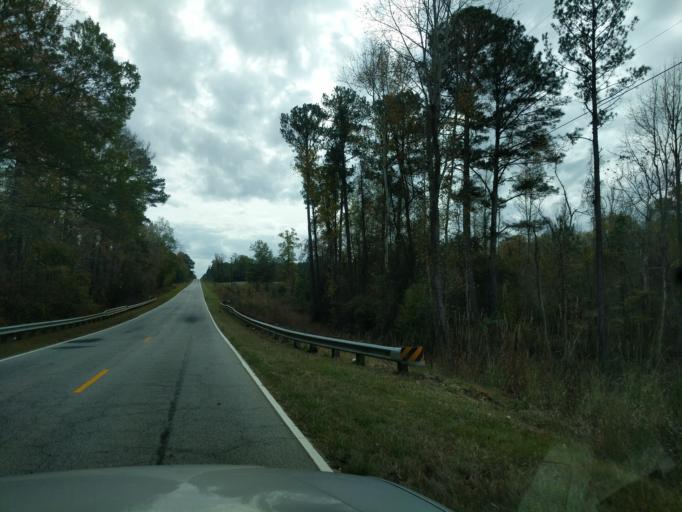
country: US
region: South Carolina
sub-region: Saluda County
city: Saluda
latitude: 34.1502
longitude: -81.8480
